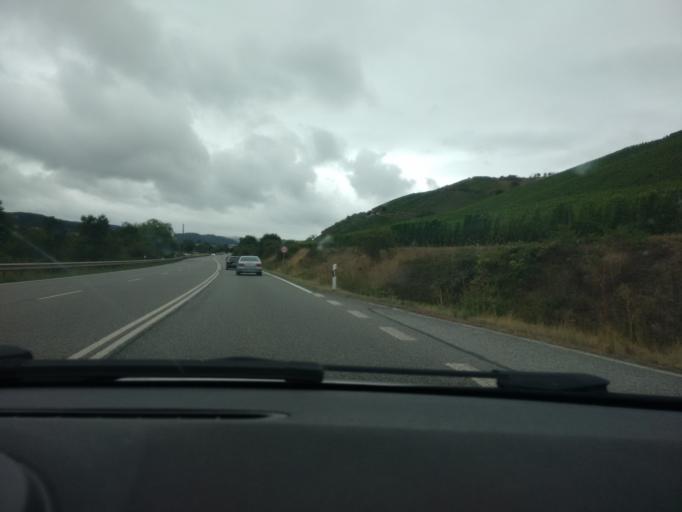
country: DE
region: Rheinland-Pfalz
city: Meddersheim
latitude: 49.7913
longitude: 7.6022
